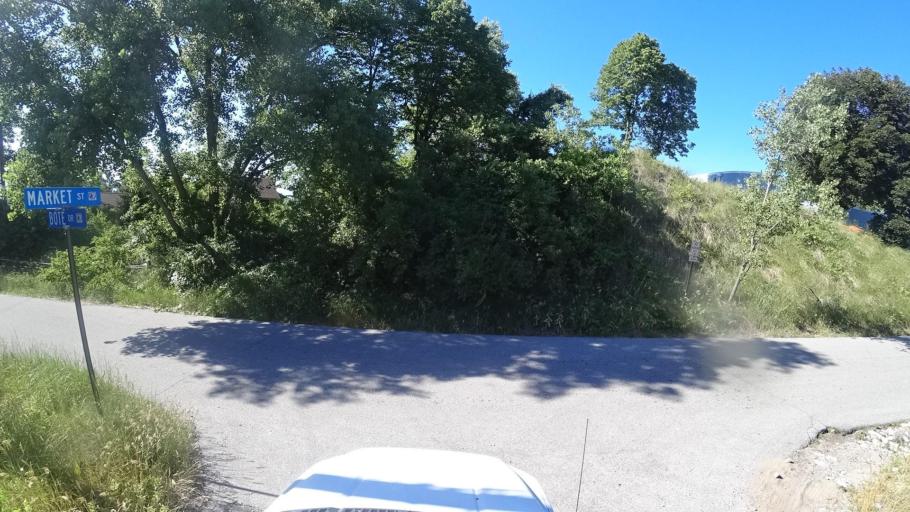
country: US
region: Indiana
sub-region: Porter County
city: Porter
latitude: 41.6568
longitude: -87.0762
